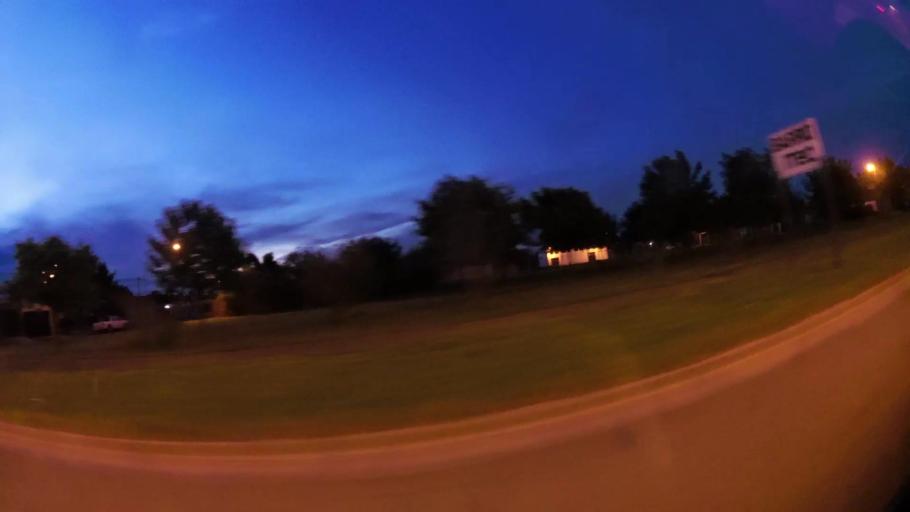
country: AR
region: Buenos Aires
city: San Nicolas de los Arroyos
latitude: -33.3578
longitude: -60.2466
